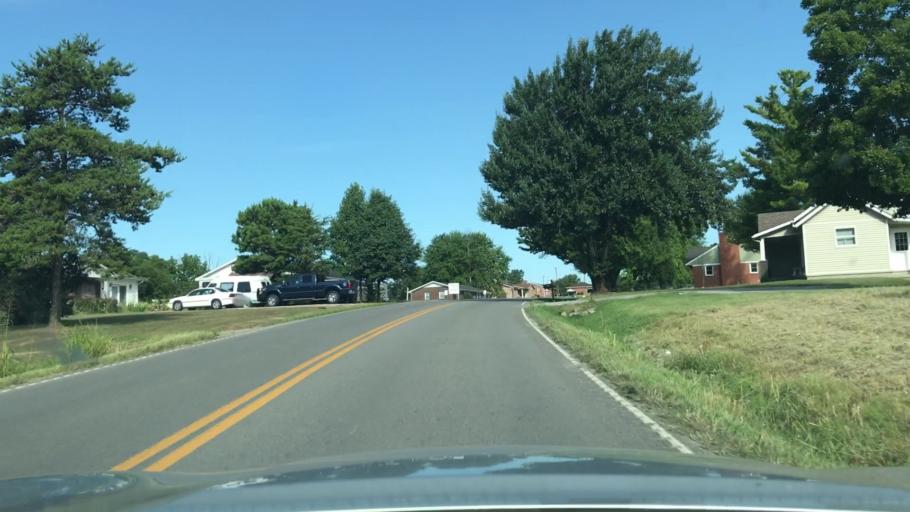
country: US
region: Kentucky
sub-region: Muhlenberg County
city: Greenville
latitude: 37.1870
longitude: -87.1653
